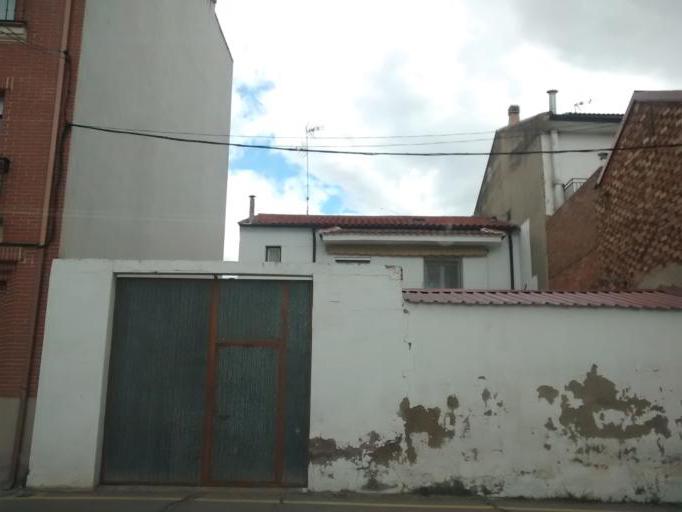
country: ES
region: La Rioja
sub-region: Provincia de La Rioja
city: Pradejon
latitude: 42.3327
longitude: -2.0681
